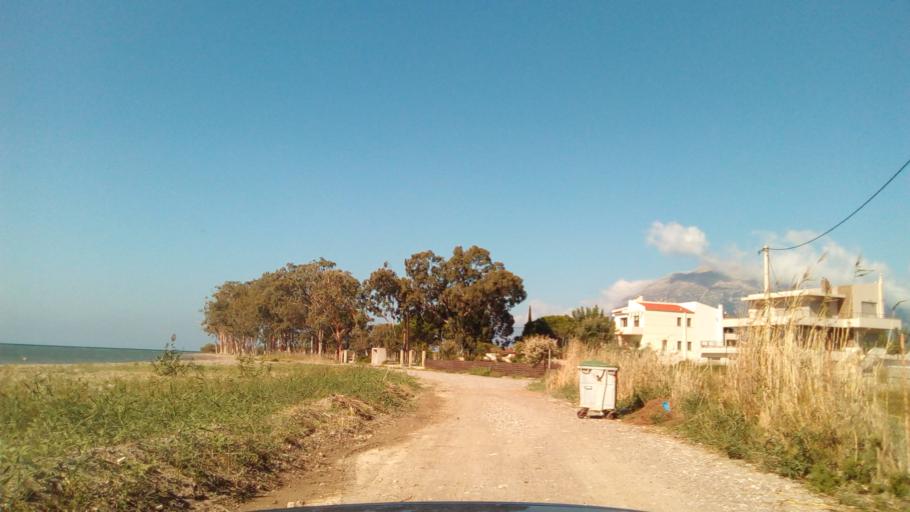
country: GR
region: West Greece
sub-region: Nomos Aitolias kai Akarnanias
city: Antirrio
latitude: 38.3321
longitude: 21.7562
